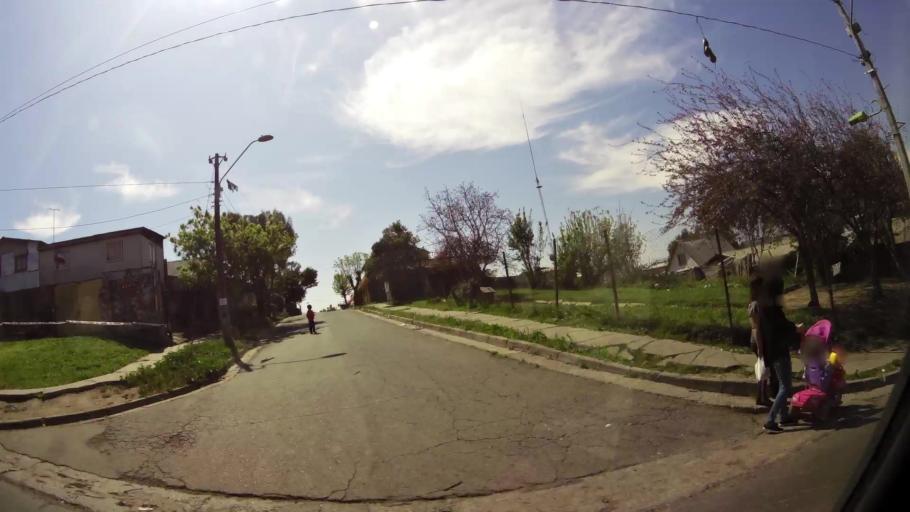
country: CL
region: Santiago Metropolitan
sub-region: Provincia de Santiago
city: Lo Prado
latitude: -33.4911
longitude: -70.7303
